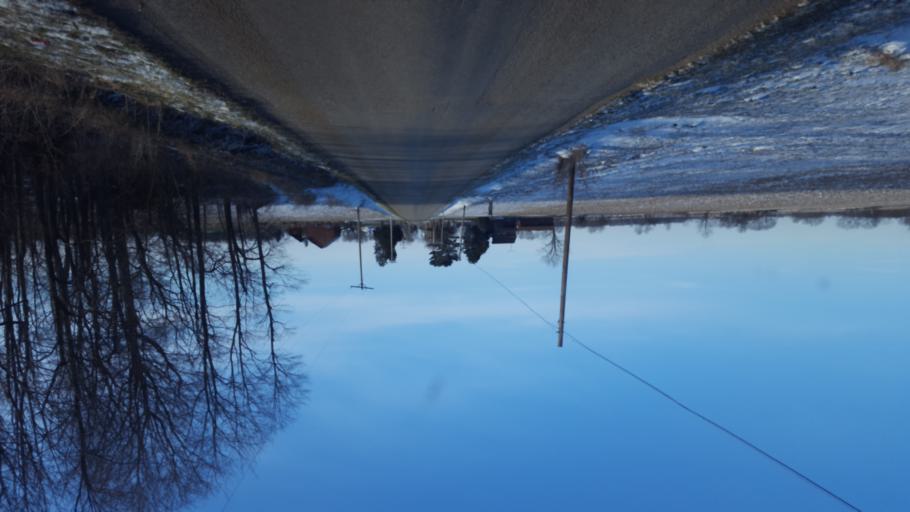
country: US
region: Ohio
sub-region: Morrow County
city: Cardington
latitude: 40.5790
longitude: -82.9188
